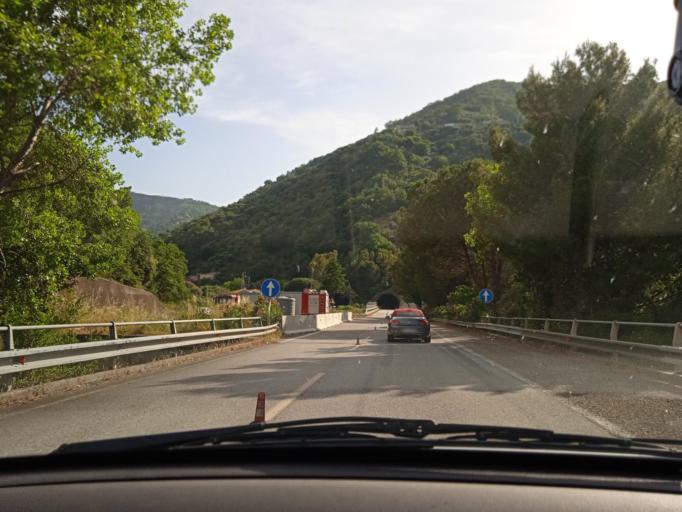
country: IT
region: Sicily
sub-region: Messina
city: Gioiosa Marea
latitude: 38.1589
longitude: 14.9062
